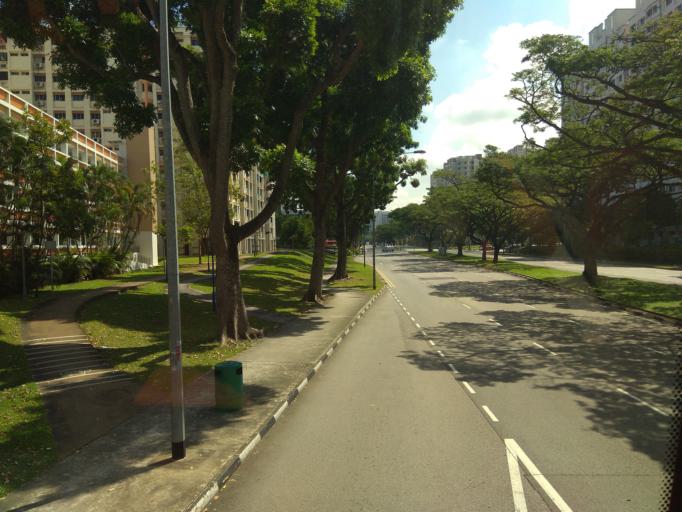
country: MY
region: Johor
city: Johor Bahru
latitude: 1.3452
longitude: 103.7008
